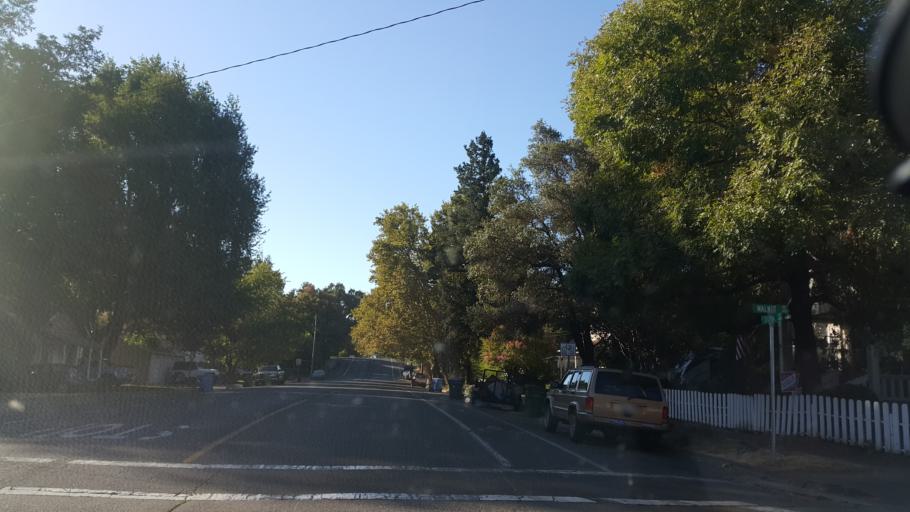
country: US
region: California
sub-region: Mendocino County
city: Ukiah
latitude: 39.1528
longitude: -123.2133
